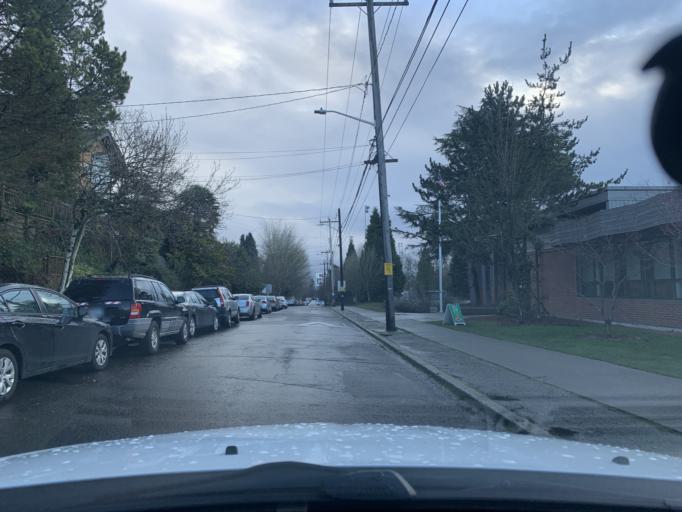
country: US
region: Washington
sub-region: King County
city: Seattle
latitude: 47.6221
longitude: -122.3048
